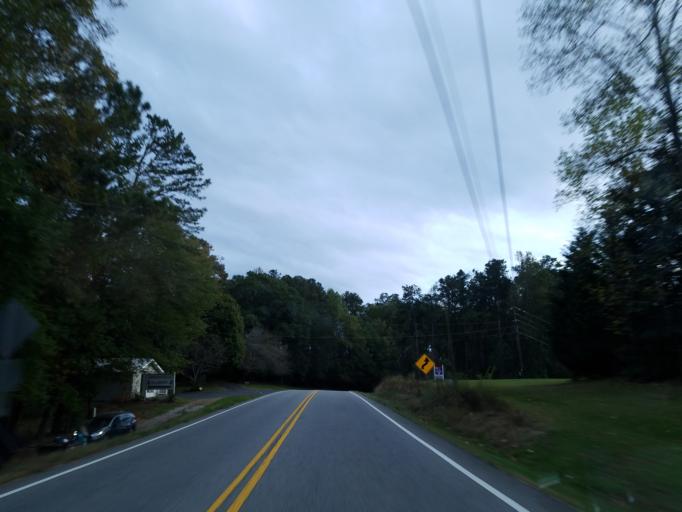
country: US
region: Georgia
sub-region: Dawson County
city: Dawsonville
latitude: 34.4058
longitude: -84.1170
